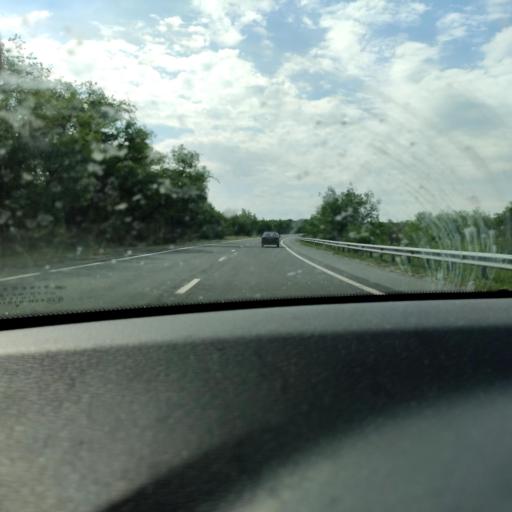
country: RU
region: Samara
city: Novosemeykino
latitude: 53.4132
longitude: 50.3370
